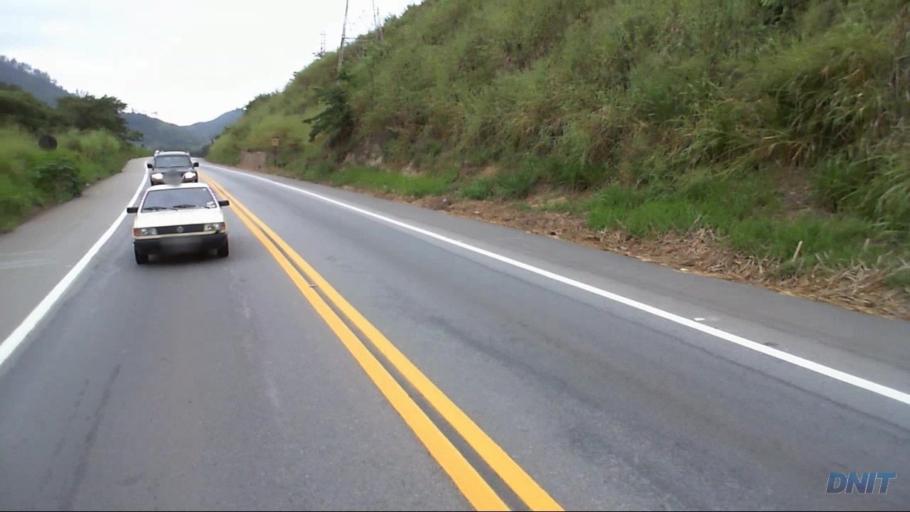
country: BR
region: Minas Gerais
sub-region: Timoteo
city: Timoteo
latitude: -19.5903
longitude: -42.7360
